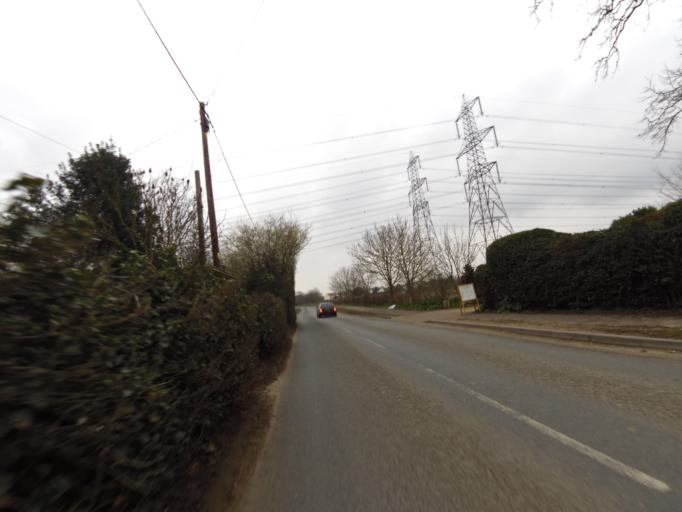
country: GB
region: England
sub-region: Suffolk
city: Wickham Market
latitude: 52.1535
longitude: 1.3938
